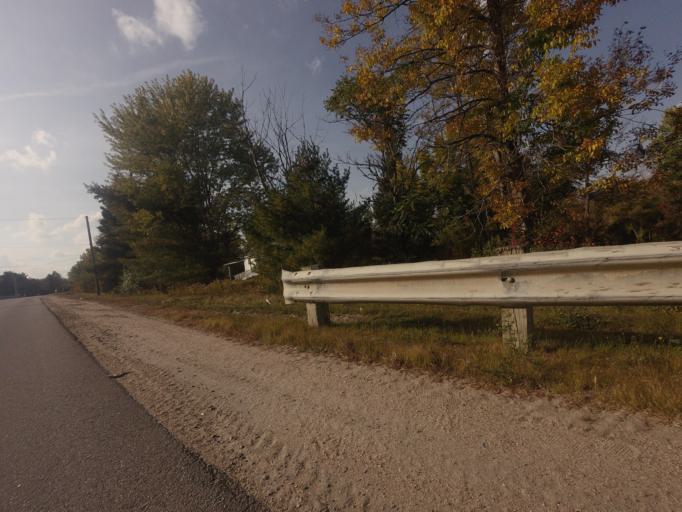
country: CA
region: Quebec
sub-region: Outaouais
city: Maniwaki
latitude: 46.3646
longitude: -75.9913
